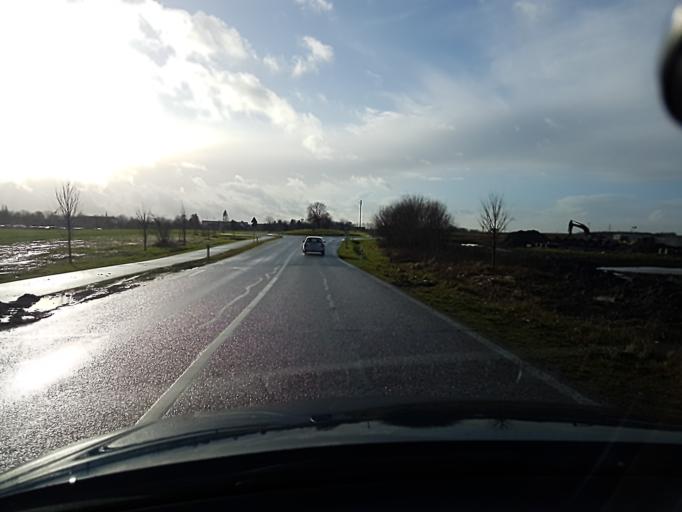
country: DE
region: Mecklenburg-Vorpommern
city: Dummerstorf
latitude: 54.0226
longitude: 12.2326
